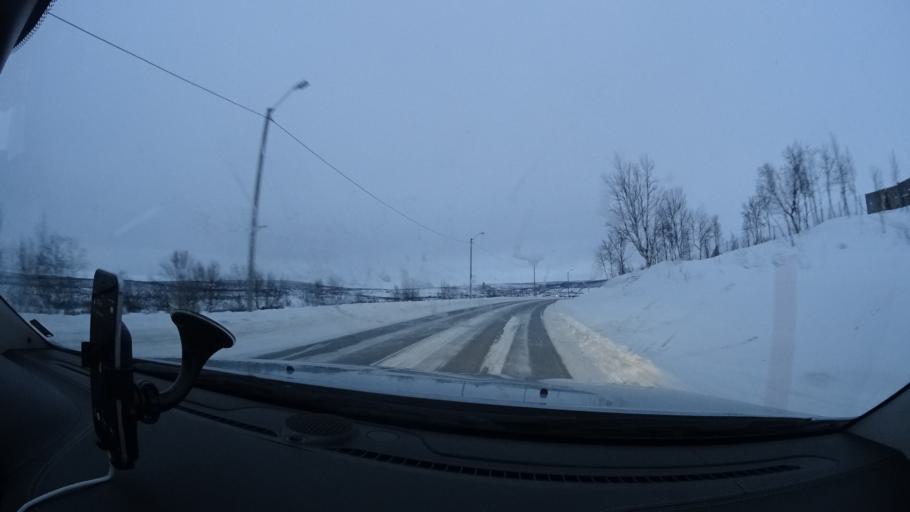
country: NO
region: Finnmark Fylke
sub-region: Kautokeino
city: Kautokeino
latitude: 69.0173
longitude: 23.0454
